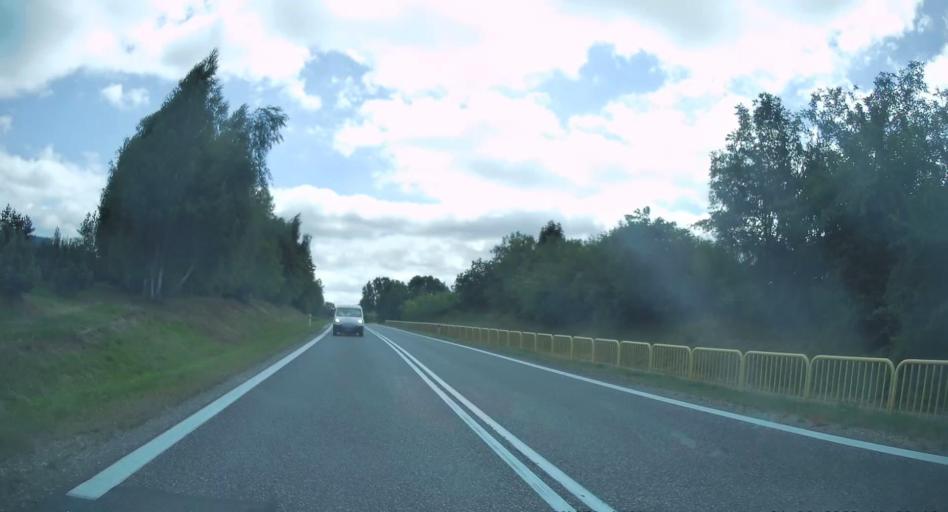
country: PL
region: Swietokrzyskie
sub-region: Powiat sandomierski
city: Loniow
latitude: 50.5927
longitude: 21.4701
